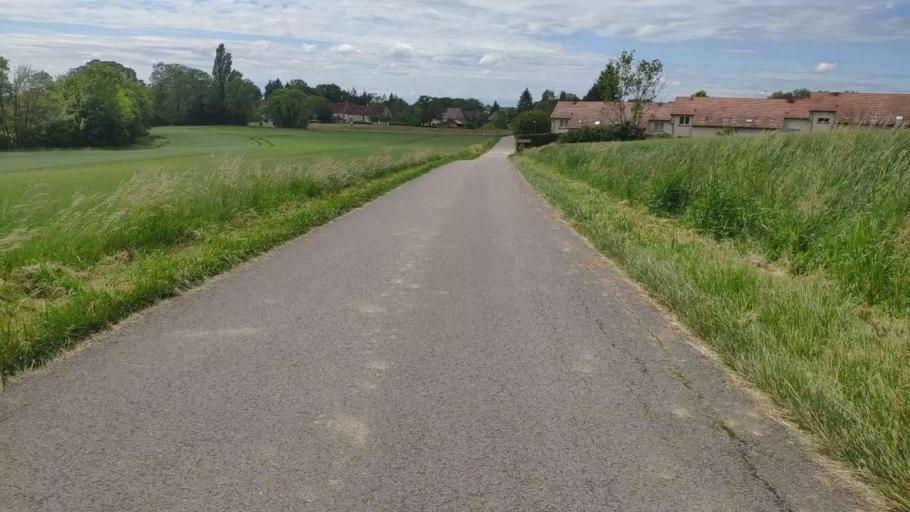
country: FR
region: Franche-Comte
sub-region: Departement du Jura
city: Bletterans
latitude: 46.7379
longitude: 5.5059
